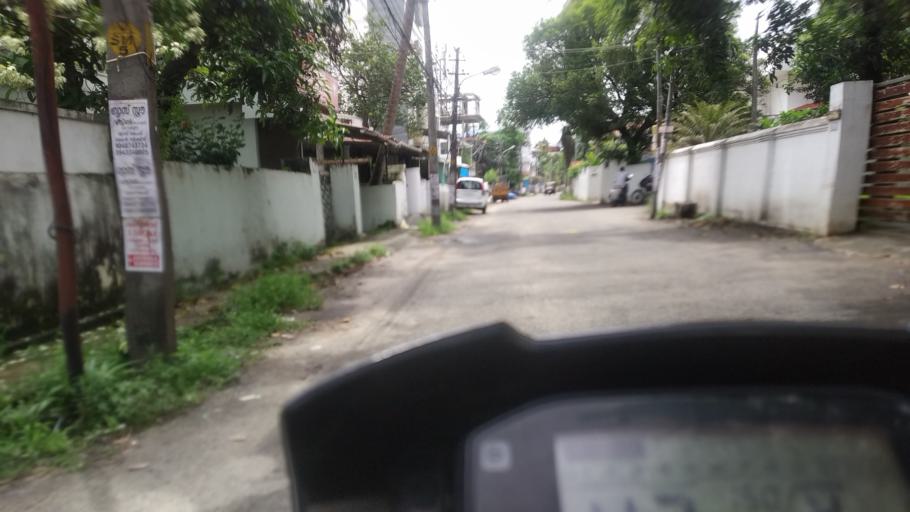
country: IN
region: Kerala
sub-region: Ernakulam
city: Elur
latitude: 10.0042
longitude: 76.2841
